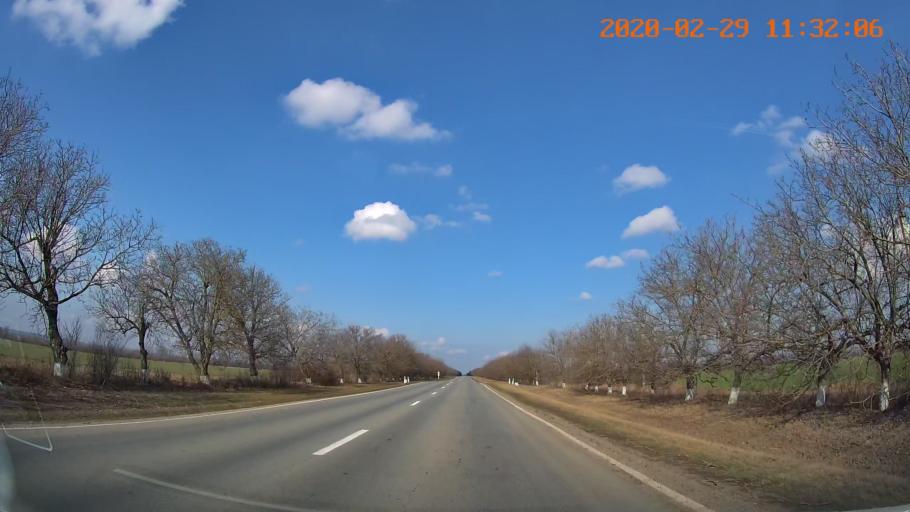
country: MD
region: Rezina
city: Saharna
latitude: 47.5331
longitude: 29.0980
